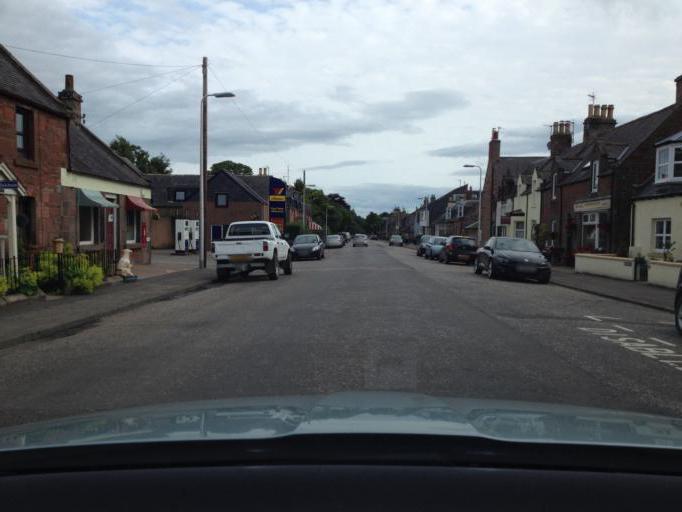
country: GB
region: Scotland
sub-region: Angus
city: Brechin
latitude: 56.8103
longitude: -2.6560
